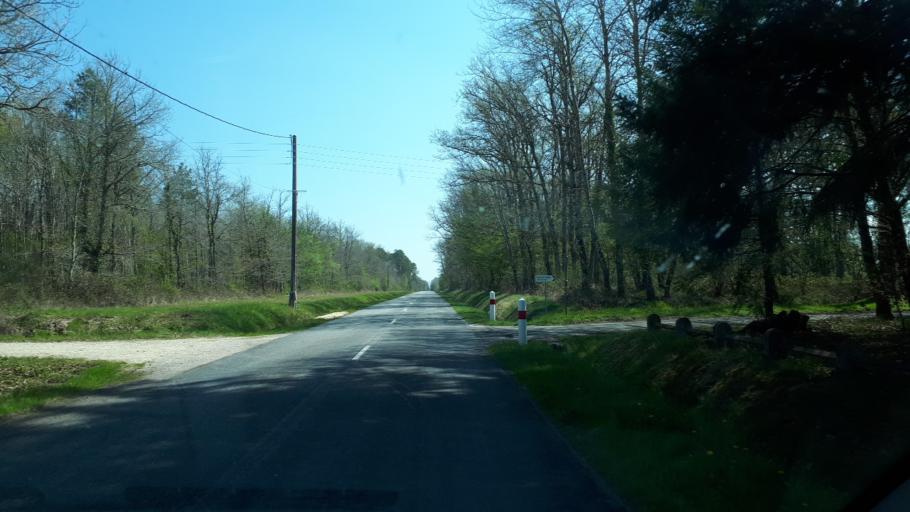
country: FR
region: Centre
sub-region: Departement du Loir-et-Cher
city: Theillay
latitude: 47.3164
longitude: 2.1289
